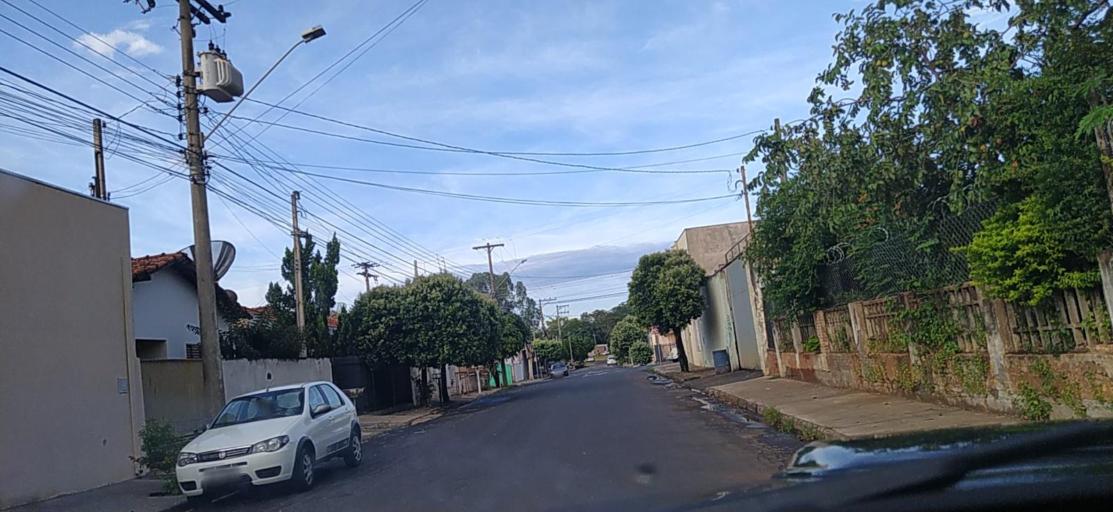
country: BR
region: Sao Paulo
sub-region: Pindorama
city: Pindorama
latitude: -21.1860
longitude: -48.9026
